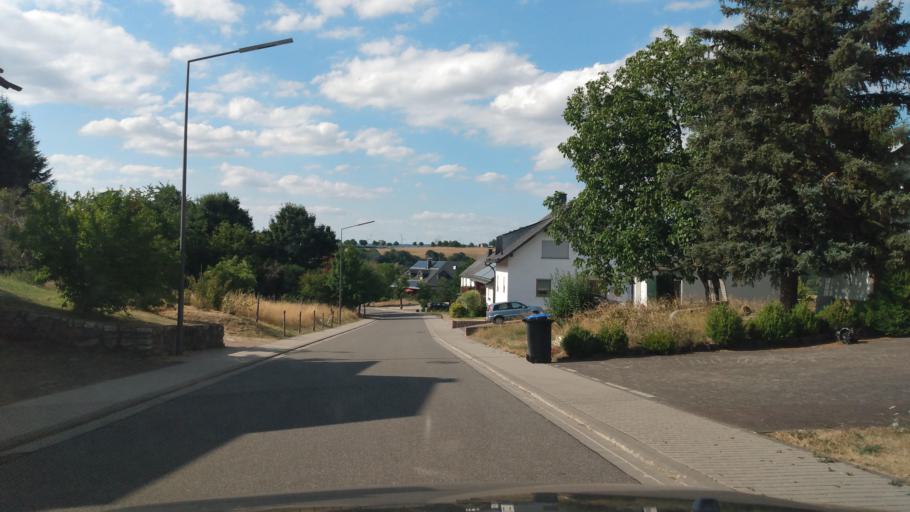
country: DE
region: Rheinland-Pfalz
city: Deuselbach
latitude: 49.7516
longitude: 7.0558
